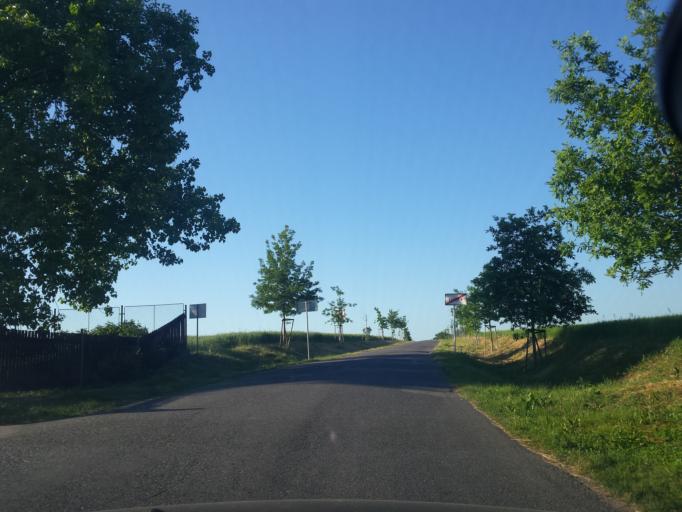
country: CZ
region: Central Bohemia
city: Mseno
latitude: 50.4324
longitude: 14.5701
